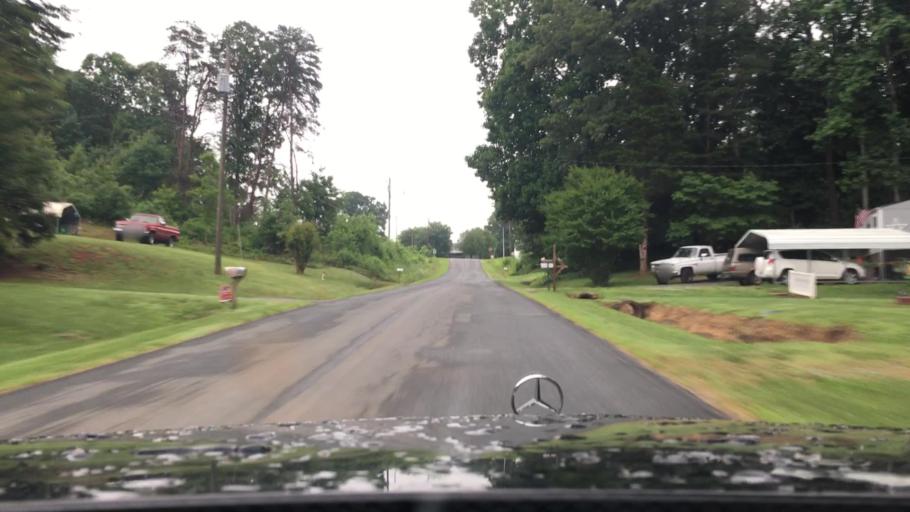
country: US
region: Virginia
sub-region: Pittsylvania County
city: Hurt
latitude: 37.0960
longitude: -79.2970
